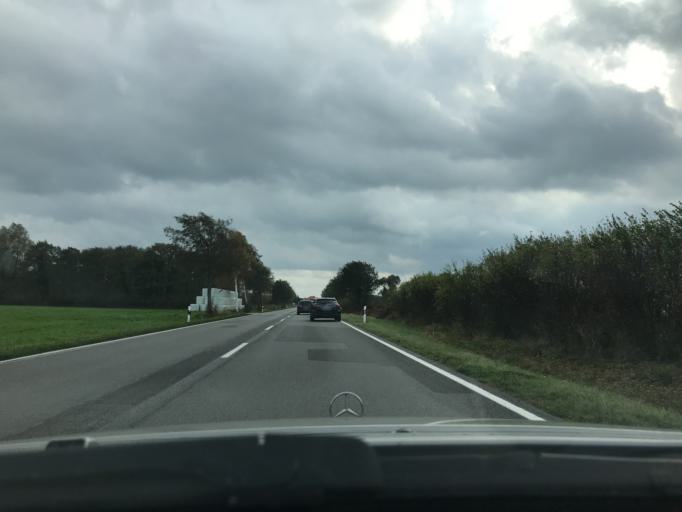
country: DE
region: Mecklenburg-Vorpommern
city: Koserow
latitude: 54.0521
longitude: 13.9915
